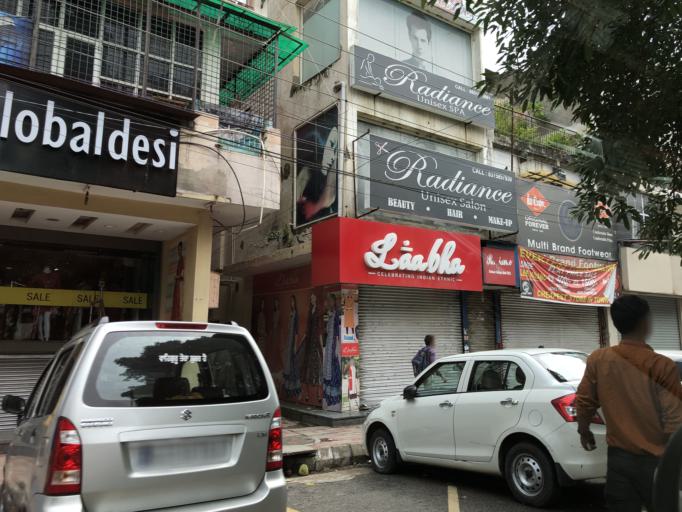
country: IN
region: NCT
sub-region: New Delhi
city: New Delhi
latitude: 28.5709
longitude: 77.2393
